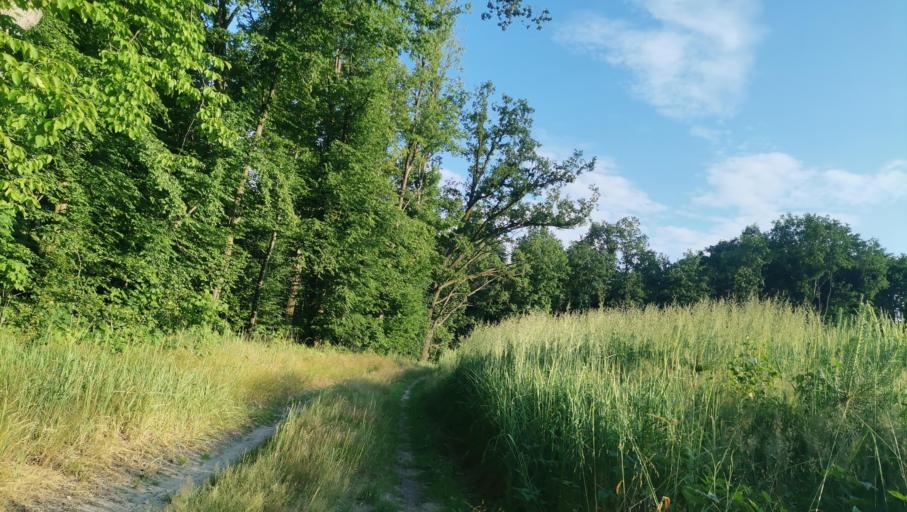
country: PL
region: Greater Poland Voivodeship
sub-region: Powiat jarocinski
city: Witaszyce
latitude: 51.9774
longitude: 17.5473
